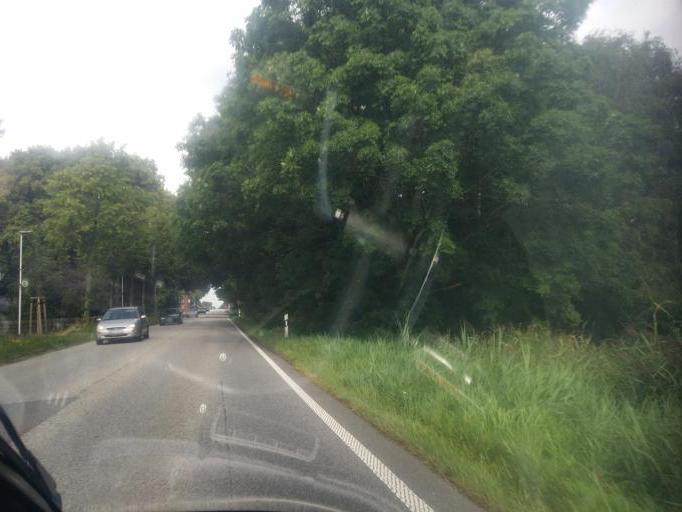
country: DE
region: Schleswig-Holstein
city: Hemmingstedt
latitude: 54.1435
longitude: 9.0691
